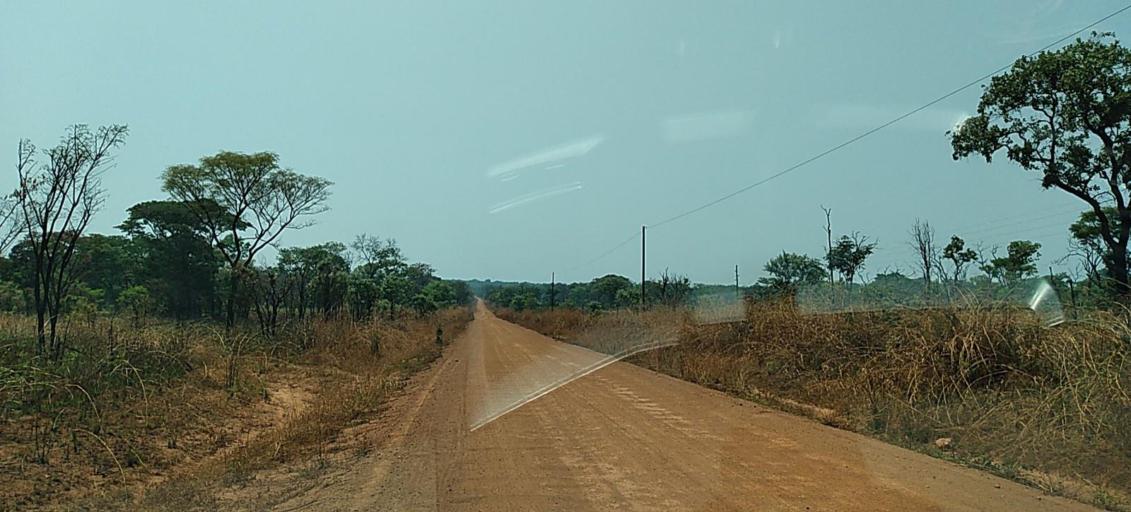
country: ZM
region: North-Western
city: Kansanshi
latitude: -11.9822
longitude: 26.7903
